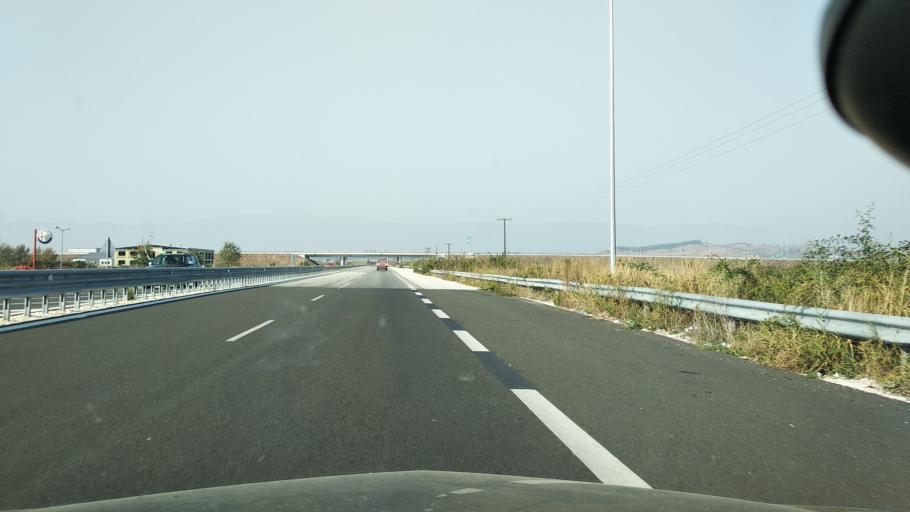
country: GR
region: Thessaly
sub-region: Trikala
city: Megalochori
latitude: 39.5667
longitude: 21.8195
